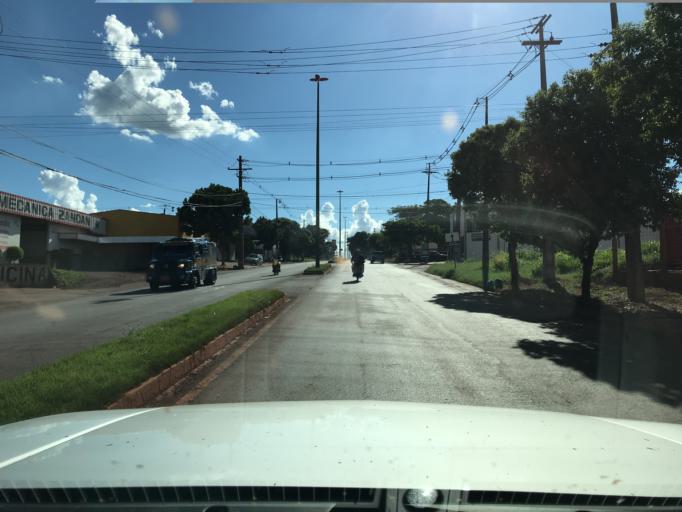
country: BR
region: Parana
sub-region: Palotina
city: Palotina
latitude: -24.2793
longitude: -53.8257
